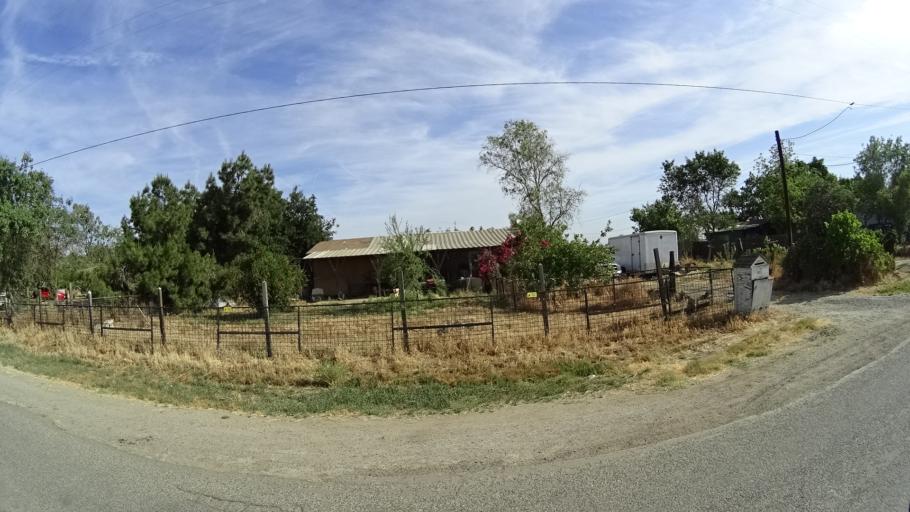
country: US
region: California
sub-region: Tulare County
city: Goshen
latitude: 36.3491
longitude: -119.4735
